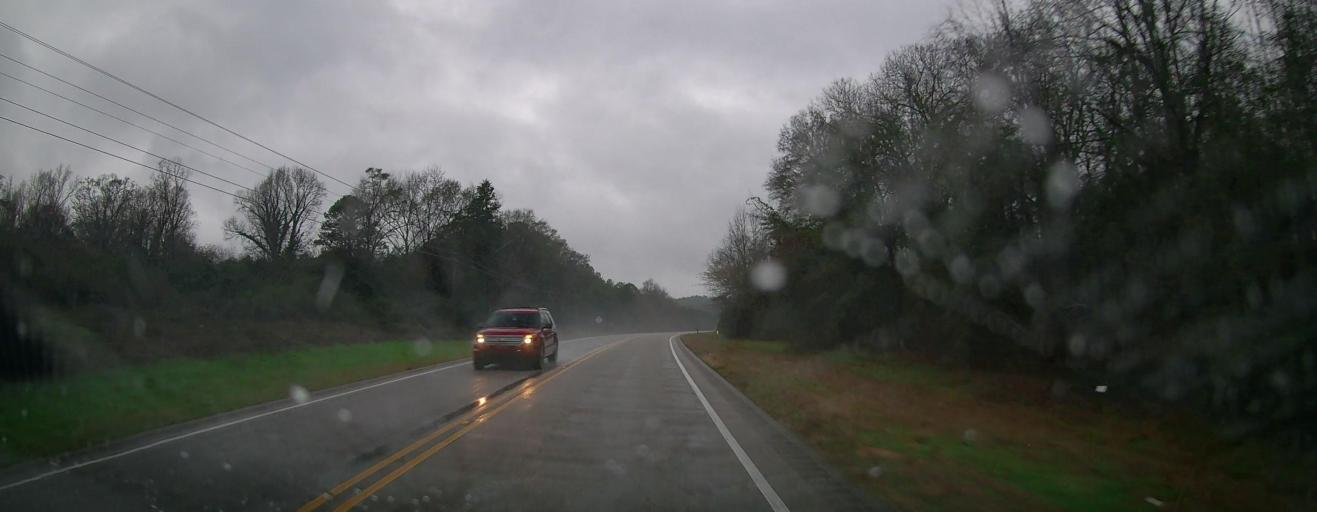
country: US
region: Alabama
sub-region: Autauga County
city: Prattville
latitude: 32.4921
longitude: -86.5737
